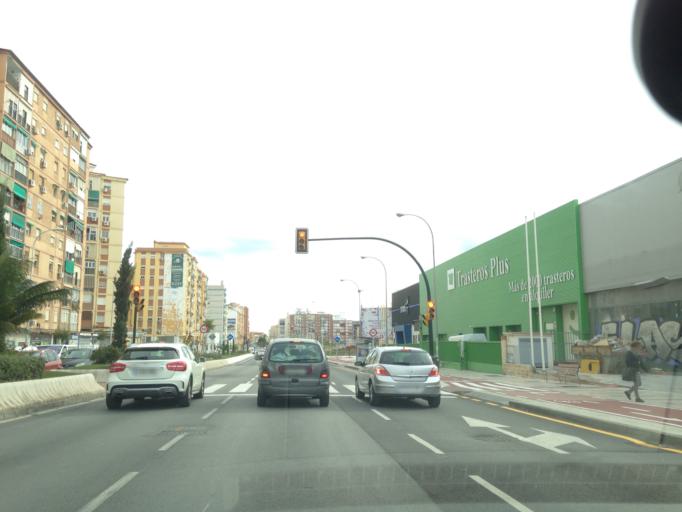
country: ES
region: Andalusia
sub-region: Provincia de Malaga
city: Malaga
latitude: 36.7087
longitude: -4.4442
